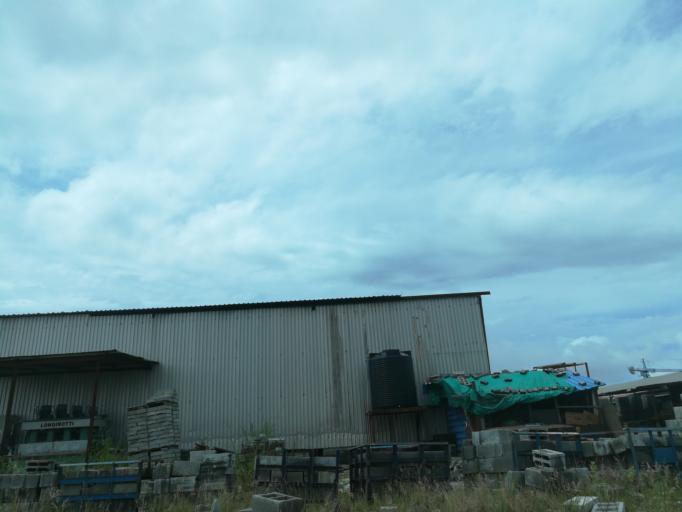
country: NG
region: Lagos
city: Lagos
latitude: 6.4121
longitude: 3.4092
